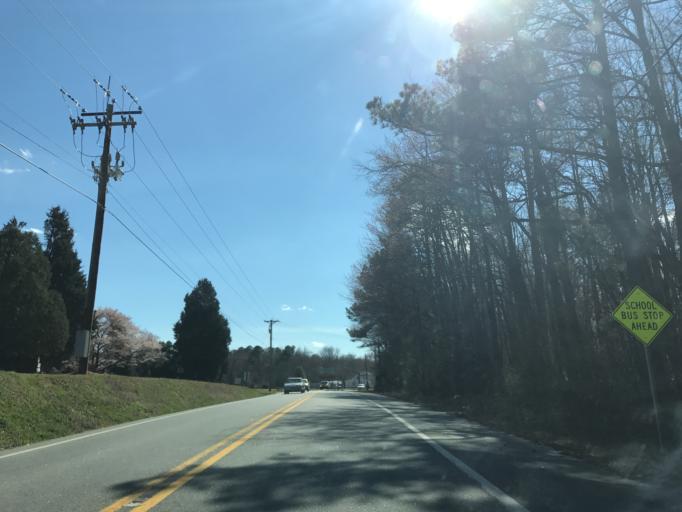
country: US
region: Maryland
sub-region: Kent County
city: Rock Hall
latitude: 39.1458
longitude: -76.2188
